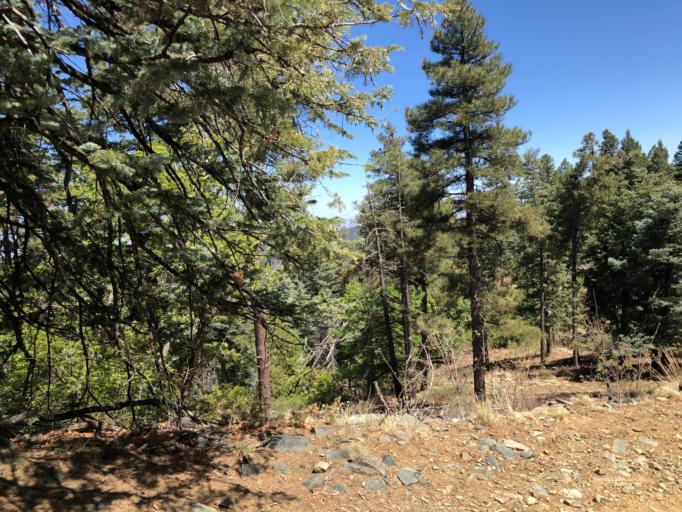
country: US
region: Arizona
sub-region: Yavapai County
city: Prescott
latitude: 34.4628
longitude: -112.4036
